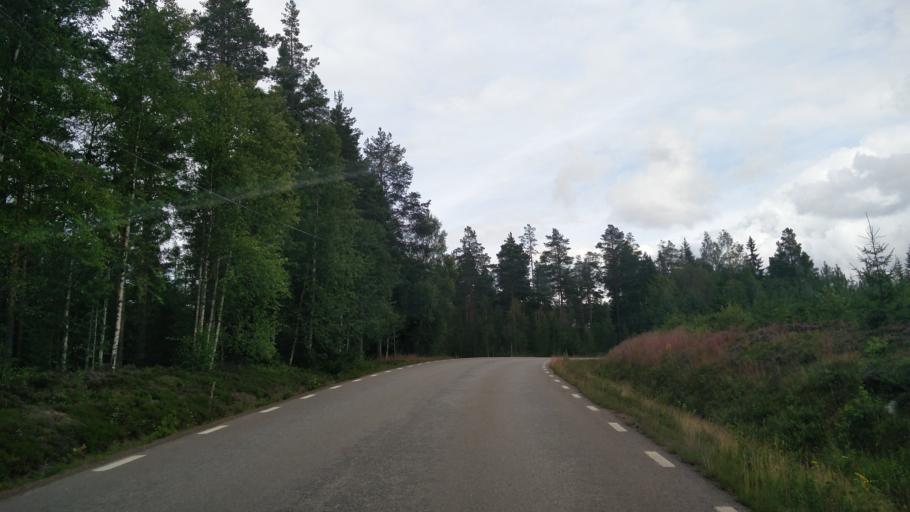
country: NO
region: Hedmark
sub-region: Trysil
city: Innbygda
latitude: 61.1766
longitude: 12.8519
